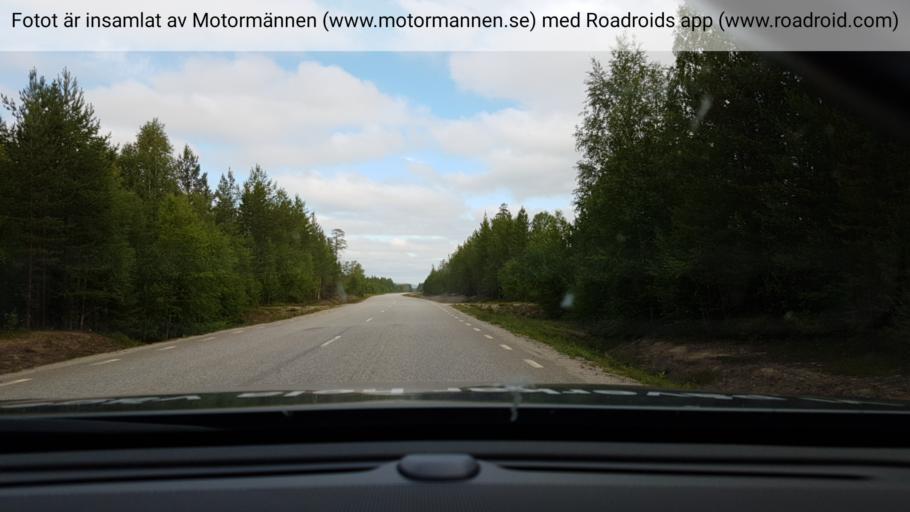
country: SE
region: Vaesterbotten
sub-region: Norsjo Kommun
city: Norsjoe
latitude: 64.5631
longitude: 19.3173
